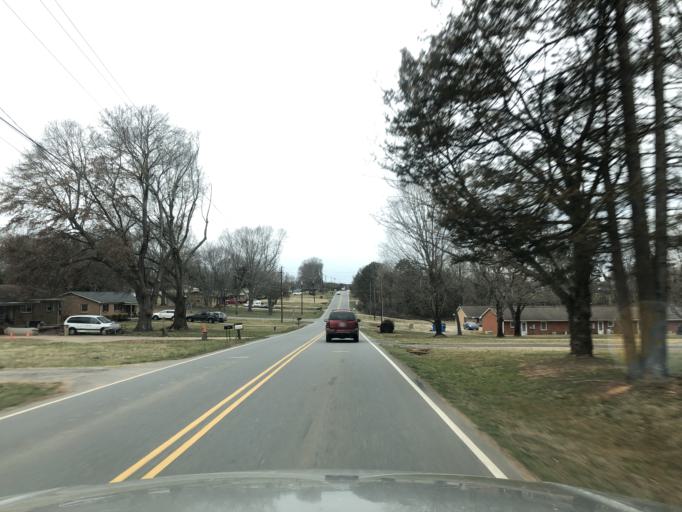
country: US
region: North Carolina
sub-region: Cleveland County
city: Shelby
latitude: 35.3284
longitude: -81.4963
